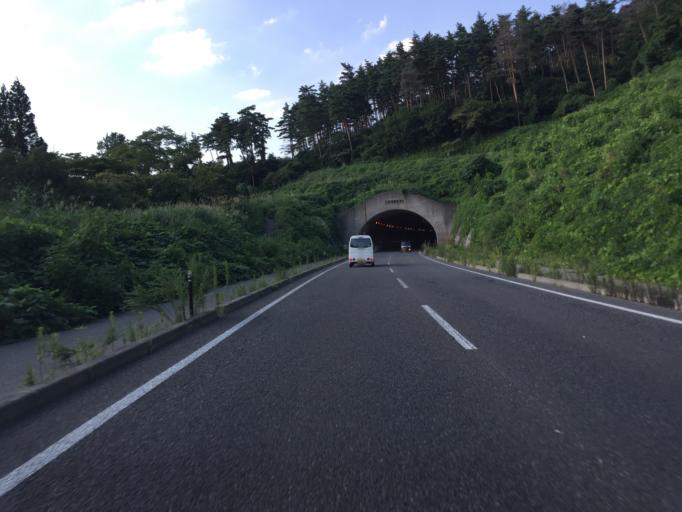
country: JP
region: Fukushima
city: Fukushima-shi
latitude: 37.7328
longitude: 140.4783
